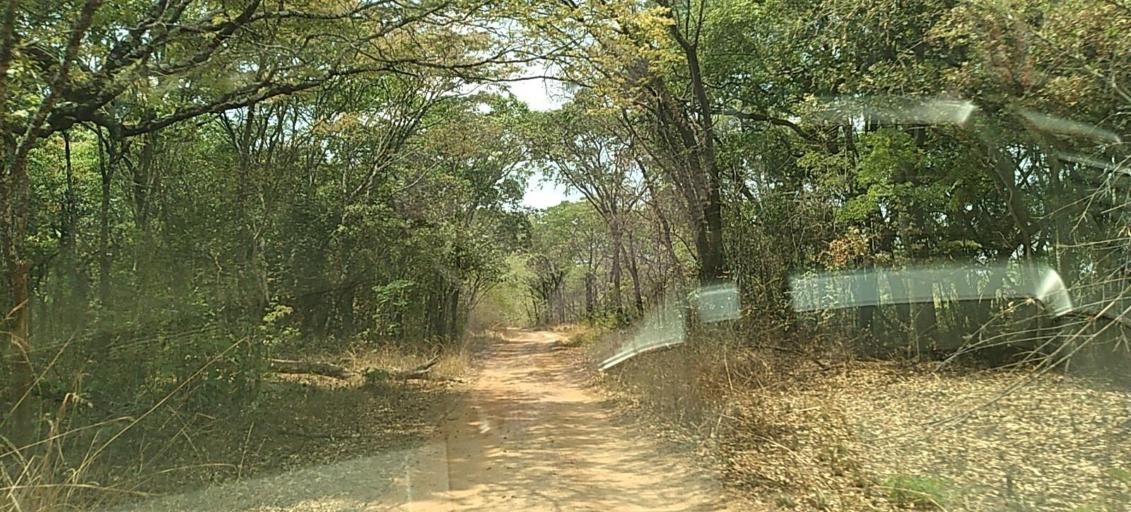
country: ZM
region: Copperbelt
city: Chingola
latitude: -12.7634
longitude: 27.7067
